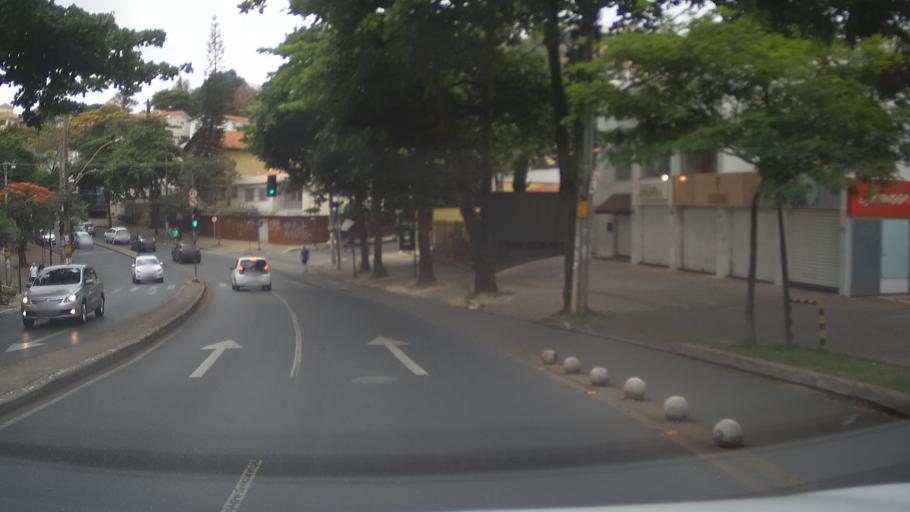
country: BR
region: Minas Gerais
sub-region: Belo Horizonte
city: Belo Horizonte
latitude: -19.9524
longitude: -43.9233
